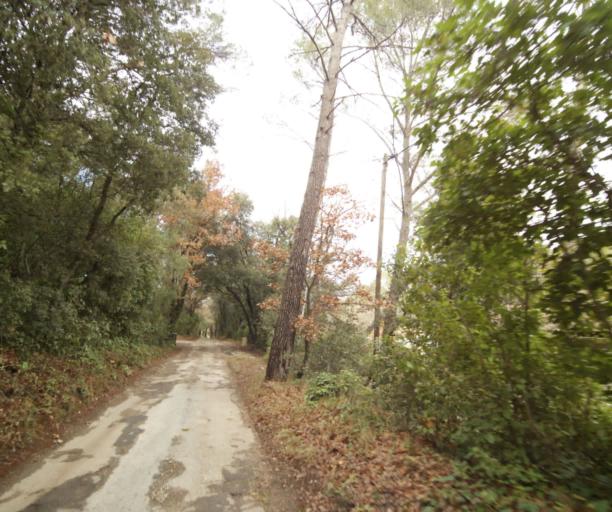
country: FR
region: Provence-Alpes-Cote d'Azur
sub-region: Departement du Var
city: Trans-en-Provence
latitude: 43.5169
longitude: 6.4919
